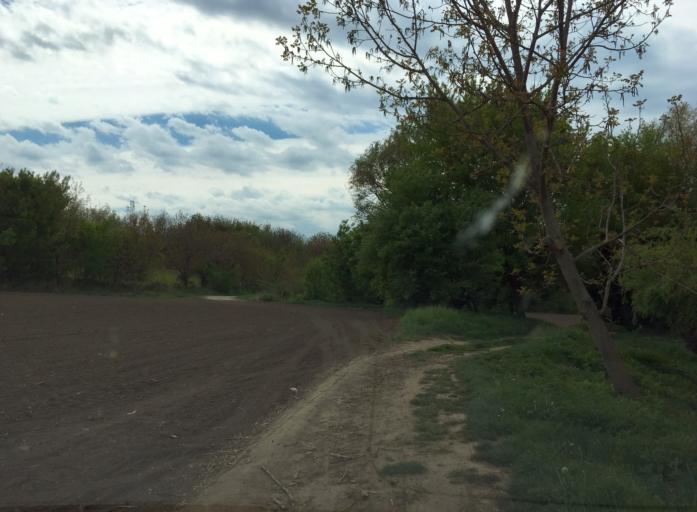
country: SK
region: Nitriansky
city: Svodin
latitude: 47.9235
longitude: 18.4190
